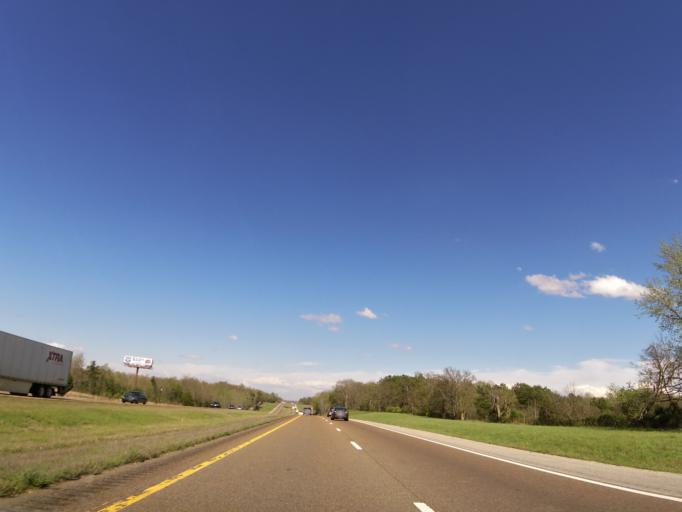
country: US
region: Tennessee
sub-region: Gibson County
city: Medina
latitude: 35.7298
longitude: -88.5973
